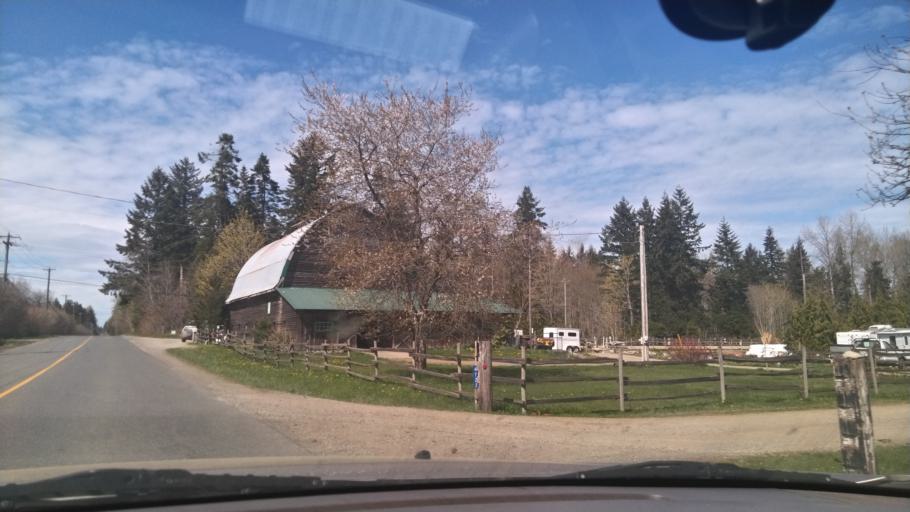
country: CA
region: British Columbia
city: Courtenay
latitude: 49.6964
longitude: -125.0126
